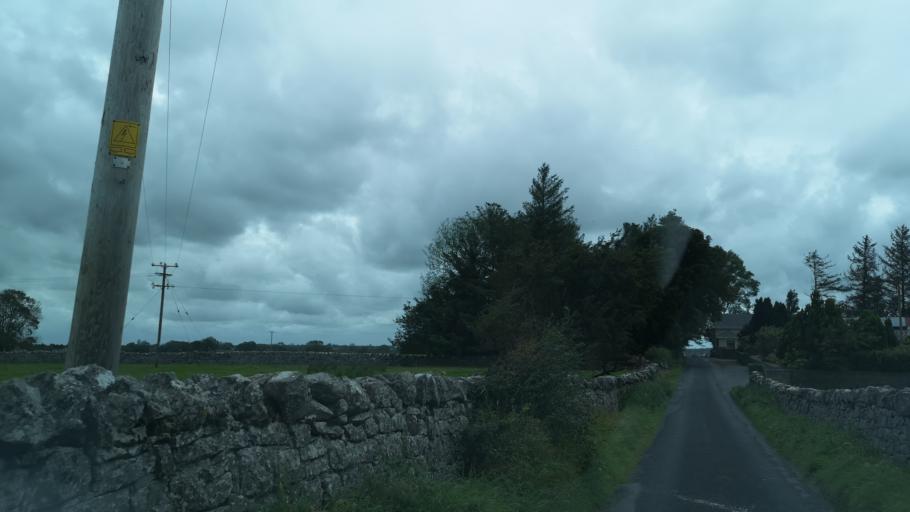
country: IE
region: Connaught
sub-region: County Galway
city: Athenry
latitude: 53.3116
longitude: -8.7445
